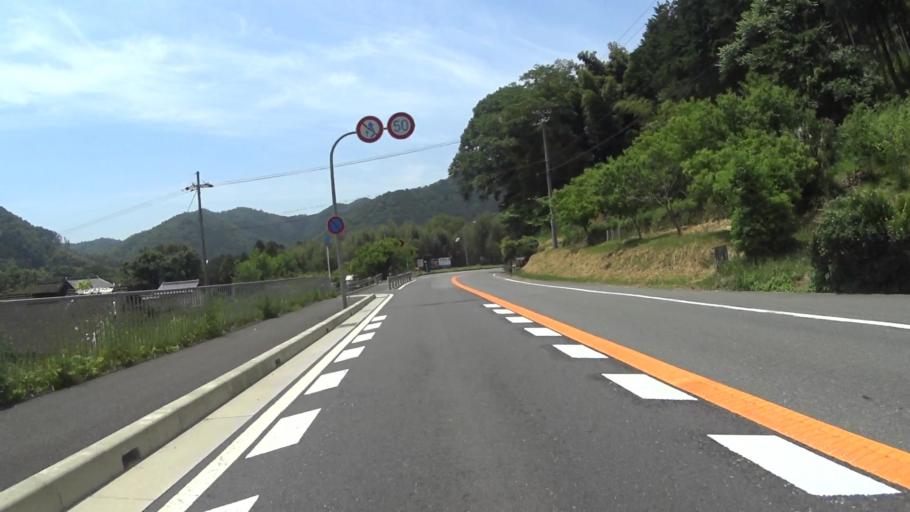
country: JP
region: Kyoto
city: Ayabe
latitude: 35.2012
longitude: 135.2496
